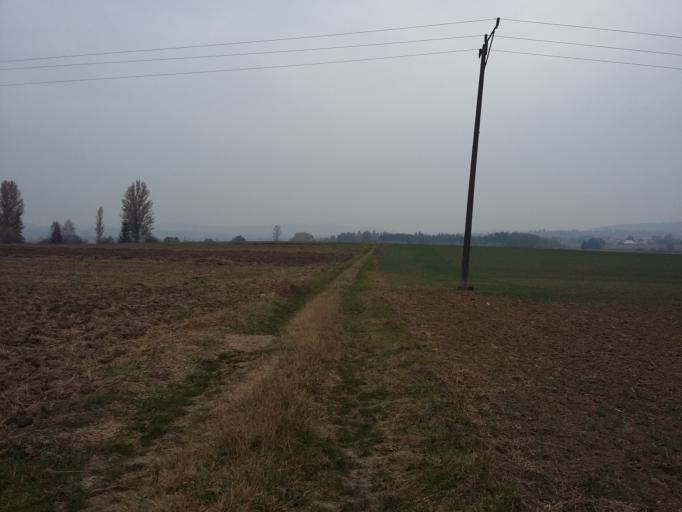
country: PL
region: Subcarpathian Voivodeship
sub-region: Powiat jasielski
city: Tarnowiec
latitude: 49.7327
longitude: 21.5657
